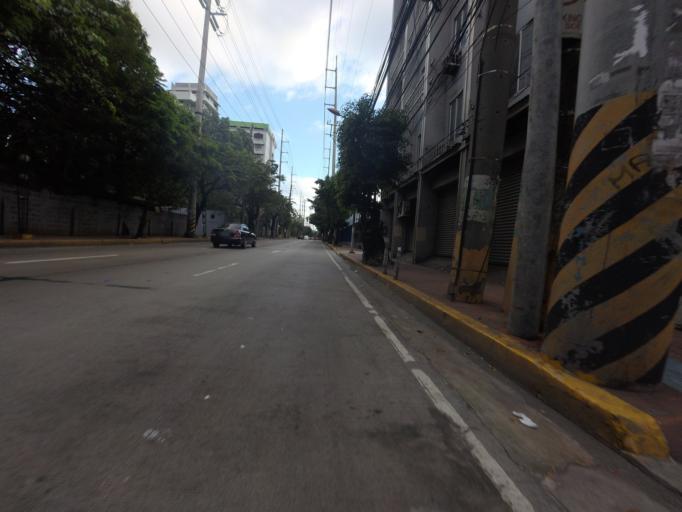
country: PH
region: Metro Manila
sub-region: City of Manila
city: Quiapo
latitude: 14.5855
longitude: 120.9861
